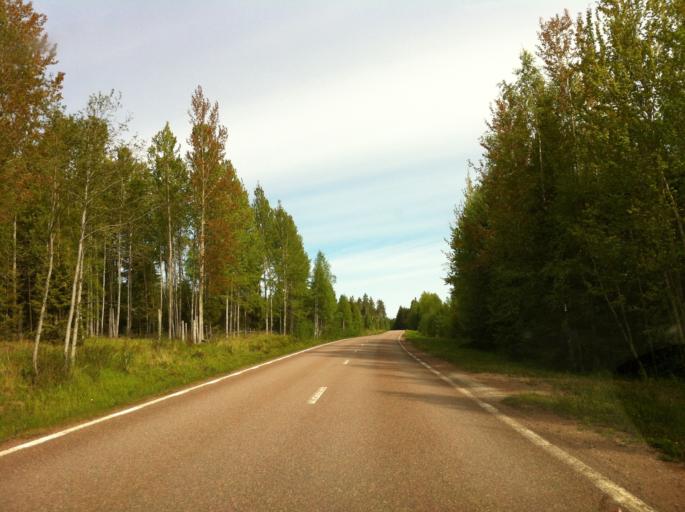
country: SE
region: Dalarna
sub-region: Leksand Municipality
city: Siljansnas
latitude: 60.8035
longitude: 14.6768
